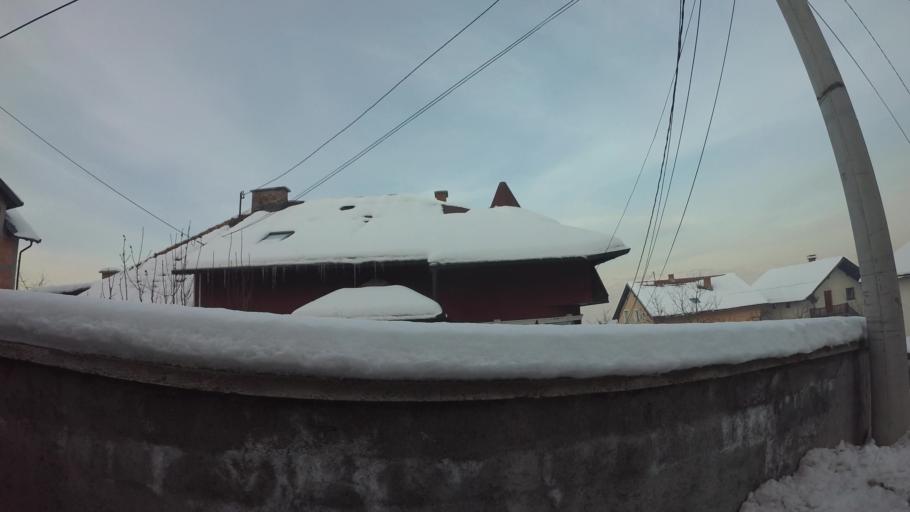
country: BA
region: Federation of Bosnia and Herzegovina
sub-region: Kanton Sarajevo
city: Sarajevo
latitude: 43.8392
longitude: 18.3578
